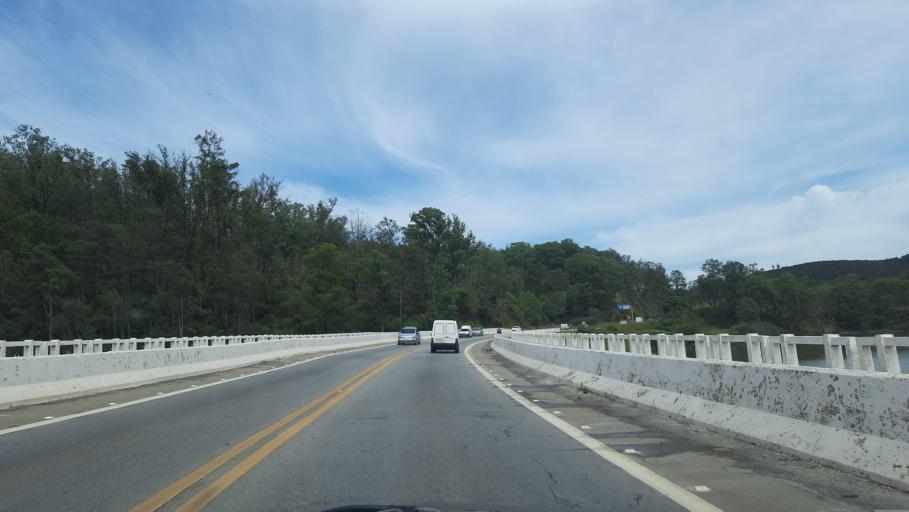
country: BR
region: Sao Paulo
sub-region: Franco Da Rocha
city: Franco da Rocha
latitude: -23.3379
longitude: -46.6609
